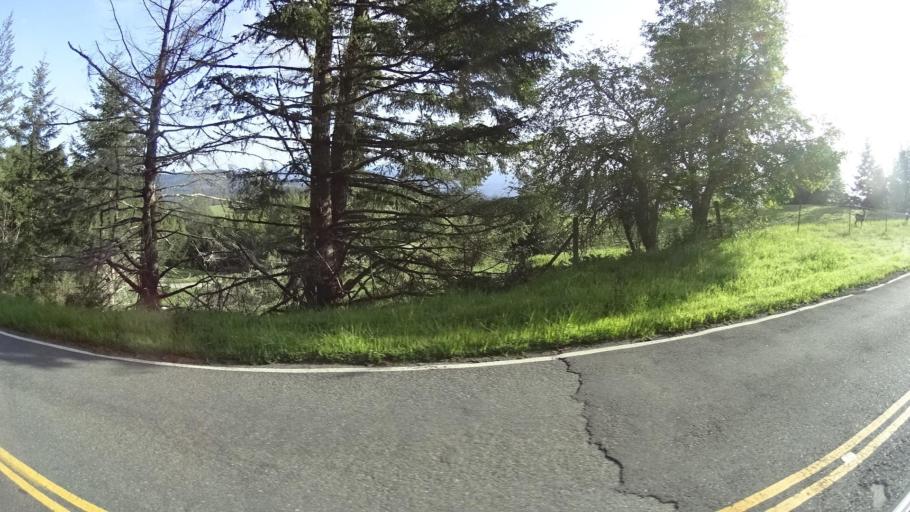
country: US
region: California
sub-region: Humboldt County
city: Blue Lake
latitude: 40.7389
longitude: -123.9509
